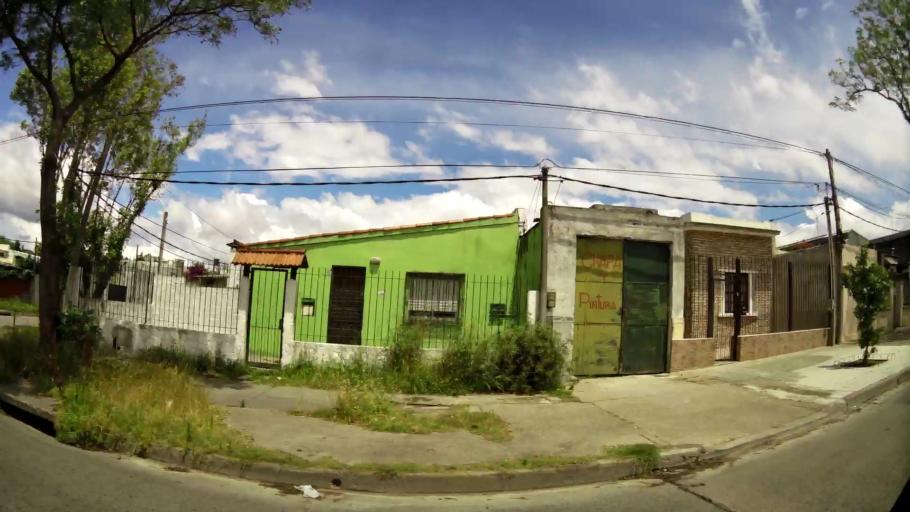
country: UY
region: Montevideo
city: Montevideo
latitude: -34.8707
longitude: -56.1293
